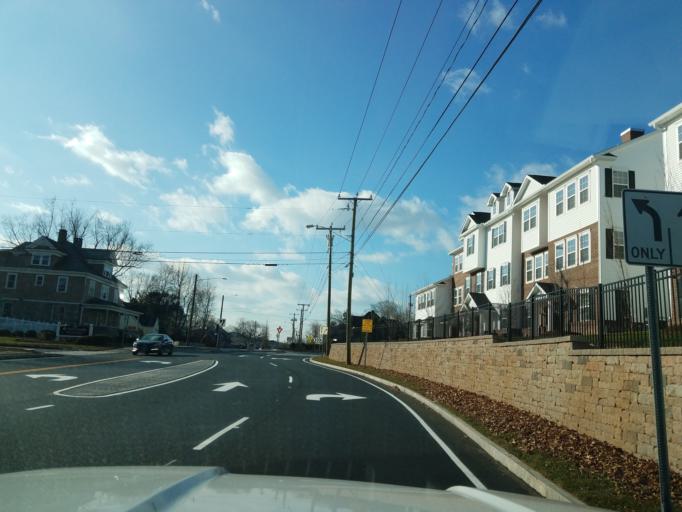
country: US
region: Connecticut
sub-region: Hartford County
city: Glastonbury
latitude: 41.7137
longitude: -72.6001
